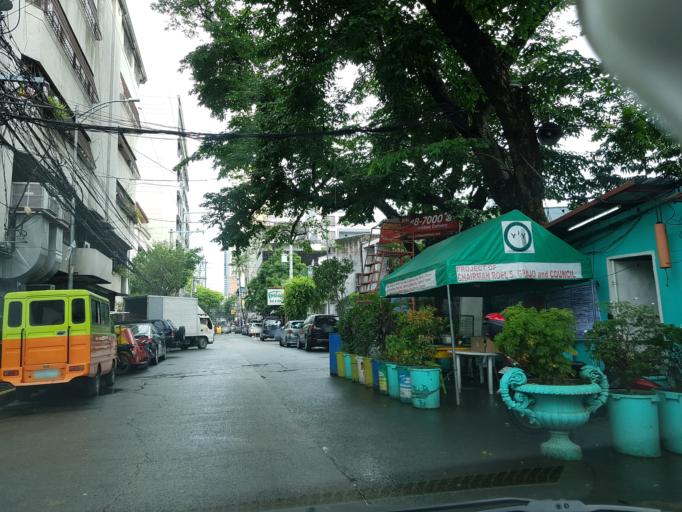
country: PH
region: Metro Manila
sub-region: City of Manila
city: Port Area
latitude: 14.5710
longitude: 120.9865
